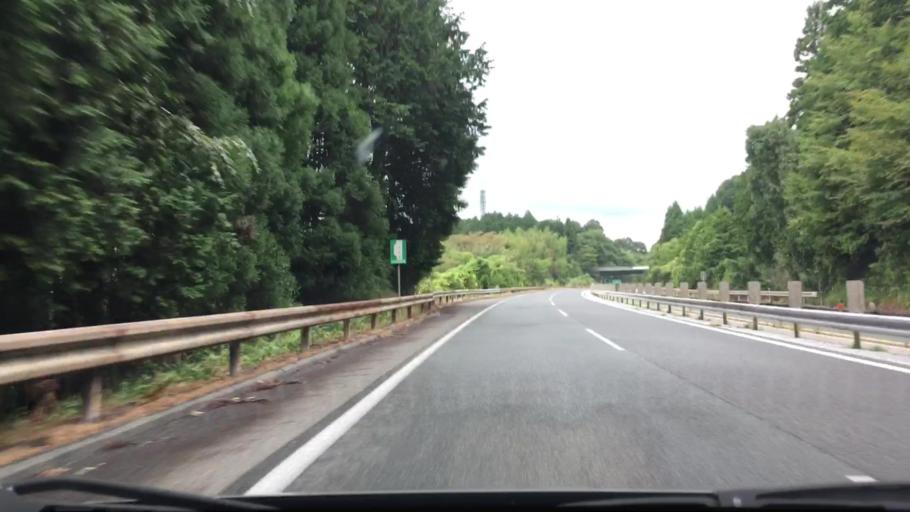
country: JP
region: Okayama
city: Niimi
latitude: 34.9291
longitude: 133.3267
